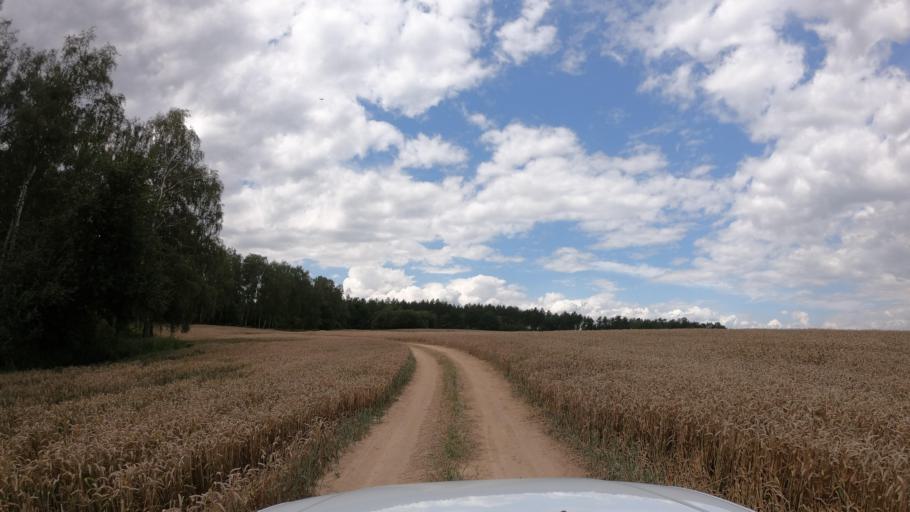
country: PL
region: West Pomeranian Voivodeship
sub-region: Powiat stargardzki
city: Dolice
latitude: 53.2020
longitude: 15.2820
